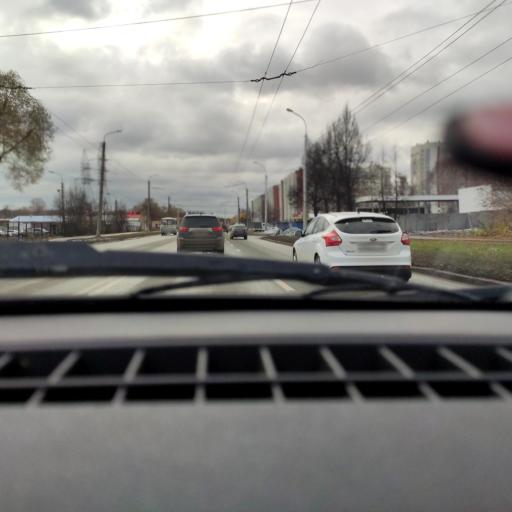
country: RU
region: Bashkortostan
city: Ufa
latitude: 54.7903
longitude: 56.1392
